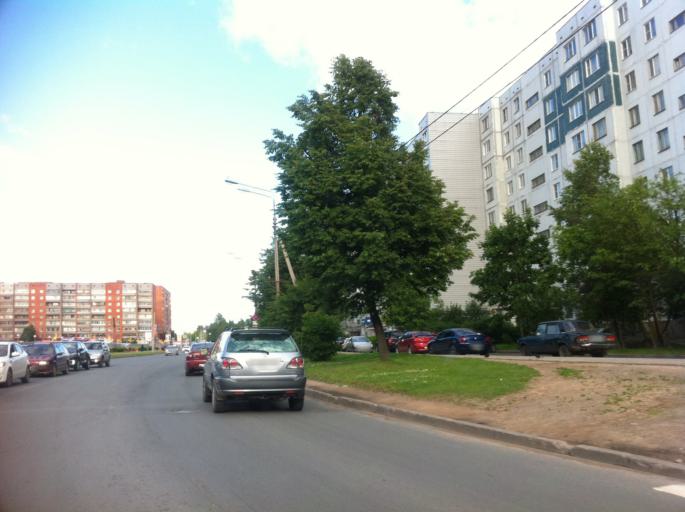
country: RU
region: Pskov
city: Pskov
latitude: 57.8195
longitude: 28.2882
